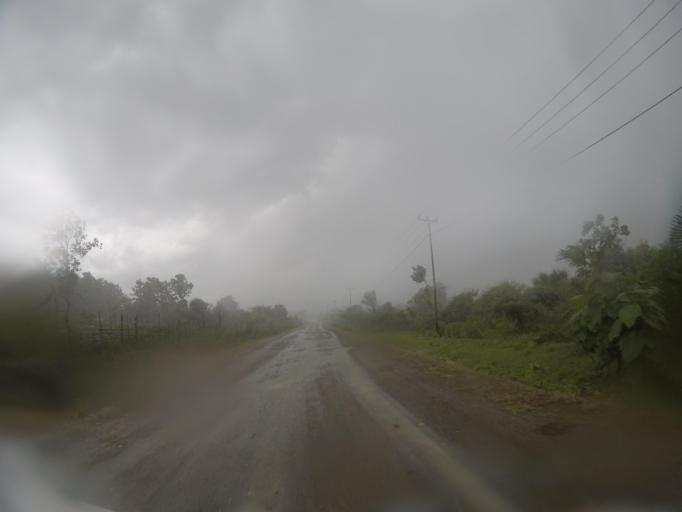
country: TL
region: Bobonaro
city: Maliana
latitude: -8.8586
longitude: 125.0907
